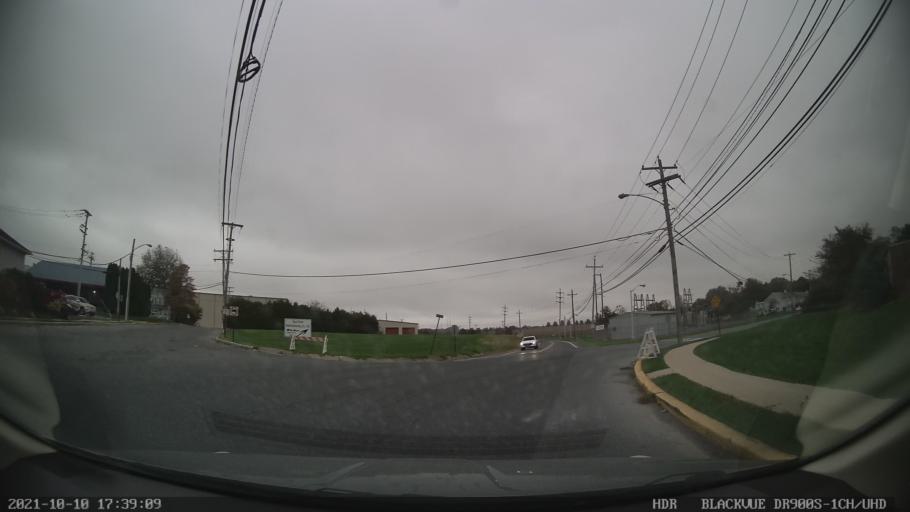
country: US
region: Pennsylvania
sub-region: Berks County
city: Topton
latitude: 40.5050
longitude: -75.6978
